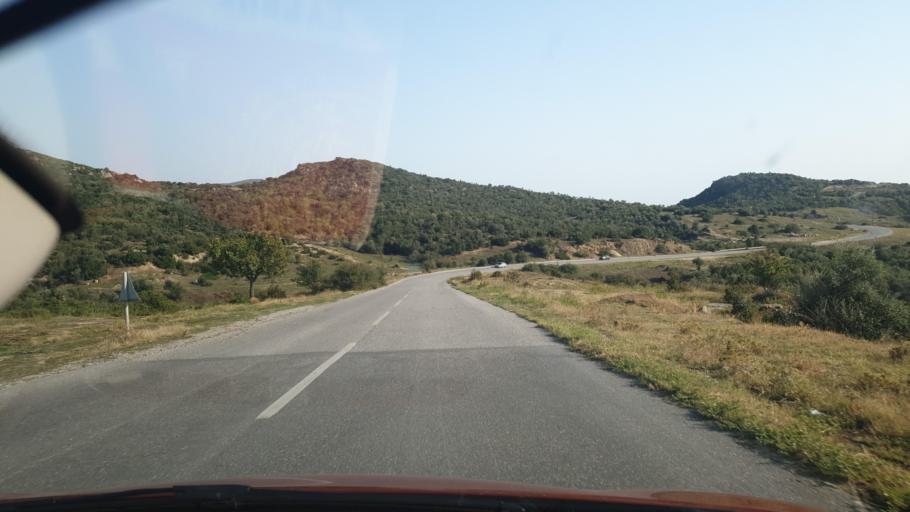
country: GR
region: Central Macedonia
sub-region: Nomos Chalkidikis
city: Sykia
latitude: 40.0202
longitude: 23.9863
